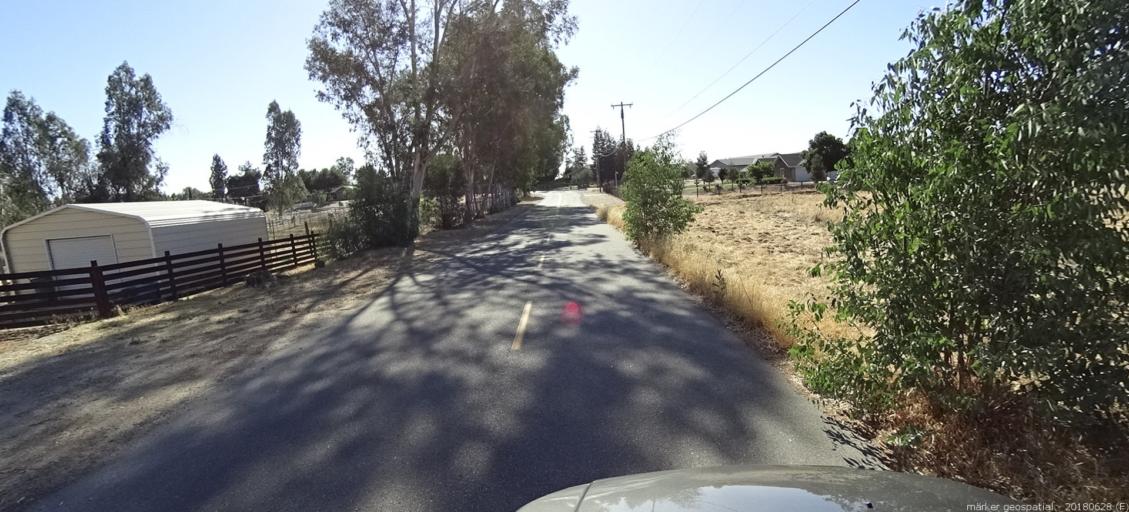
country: US
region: California
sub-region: Madera County
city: Bonadelle Ranchos-Madera Ranchos
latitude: 36.9695
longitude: -119.8916
